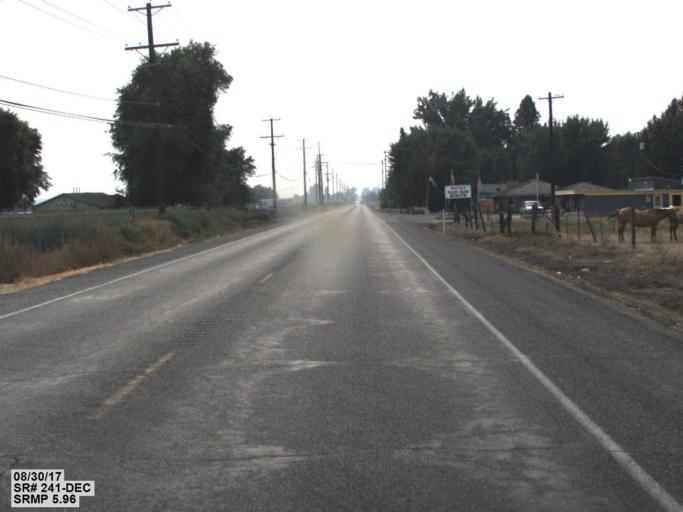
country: US
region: Washington
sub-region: Yakima County
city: Sunnyside
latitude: 46.2980
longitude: -119.9991
